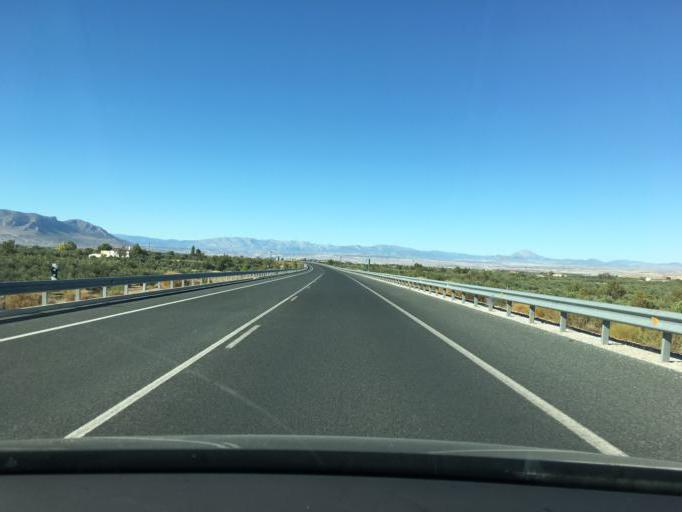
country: ES
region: Andalusia
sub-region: Provincia de Granada
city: Caniles
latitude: 37.4675
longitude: -2.7371
